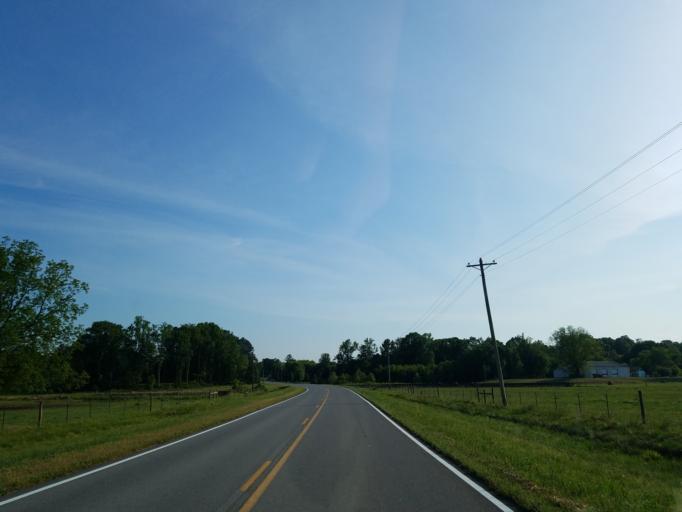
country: US
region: Georgia
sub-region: Chattooga County
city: Trion
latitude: 34.4973
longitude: -85.2471
